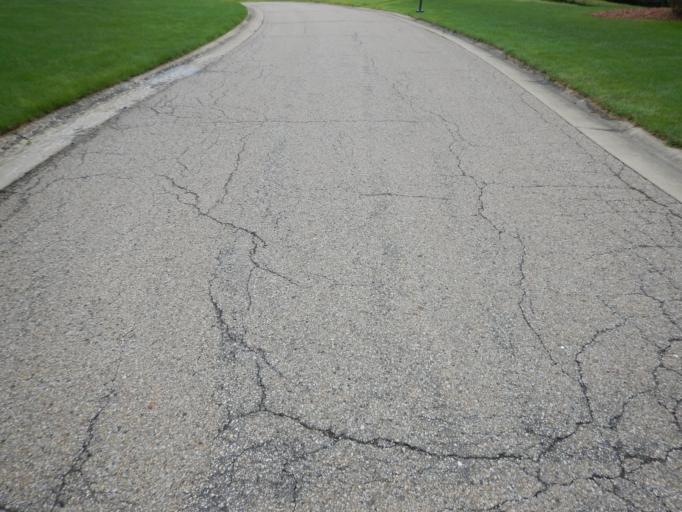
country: US
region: Ohio
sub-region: Muskingum County
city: North Zanesville
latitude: 39.9683
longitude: -82.0285
